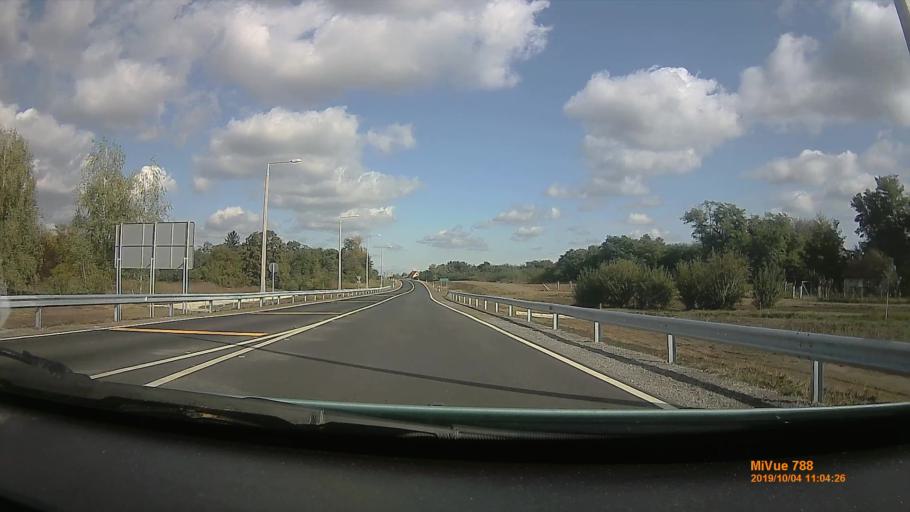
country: HU
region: Szabolcs-Szatmar-Bereg
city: Nyirtelek
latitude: 47.9878
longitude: 21.6707
